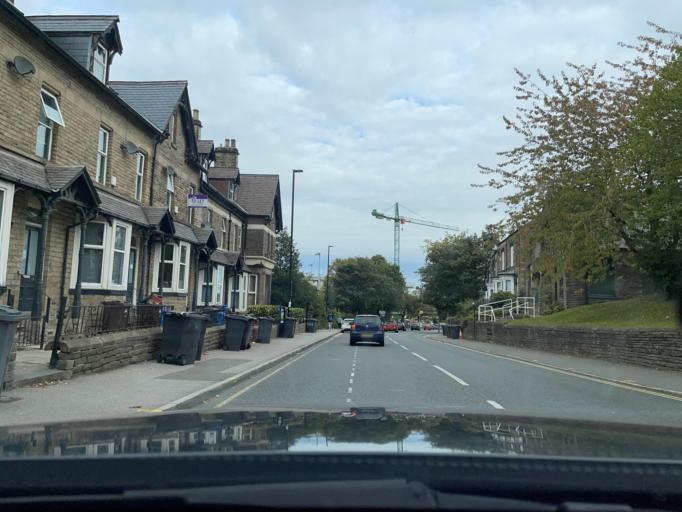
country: GB
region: England
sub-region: Sheffield
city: Sheffield
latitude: 53.3794
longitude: -1.4974
